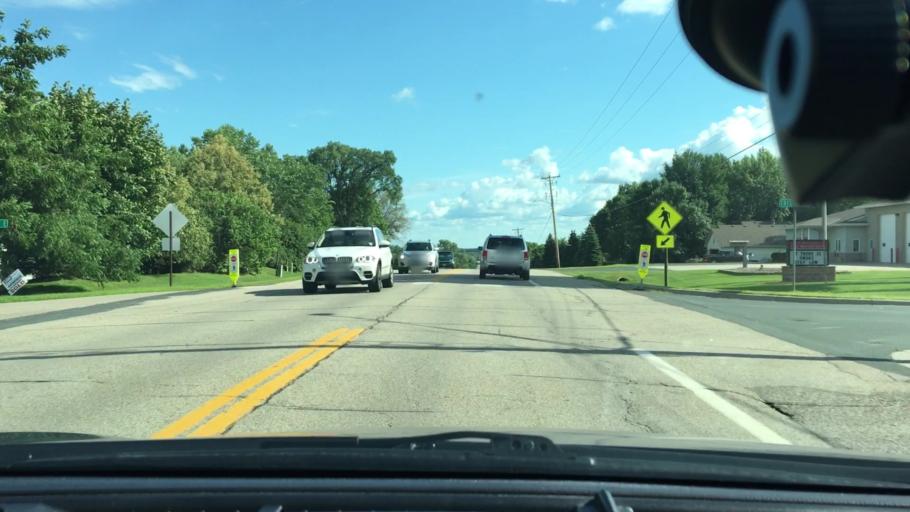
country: US
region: Minnesota
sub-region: Hennepin County
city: Saint Bonifacius
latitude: 44.9125
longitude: -93.7473
